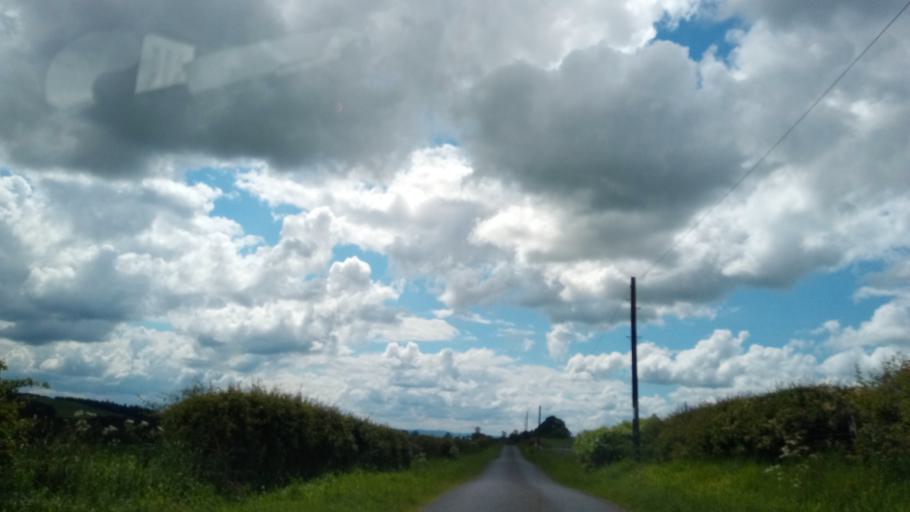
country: GB
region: Scotland
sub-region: The Scottish Borders
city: Coldstream
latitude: 55.5809
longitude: -2.3115
